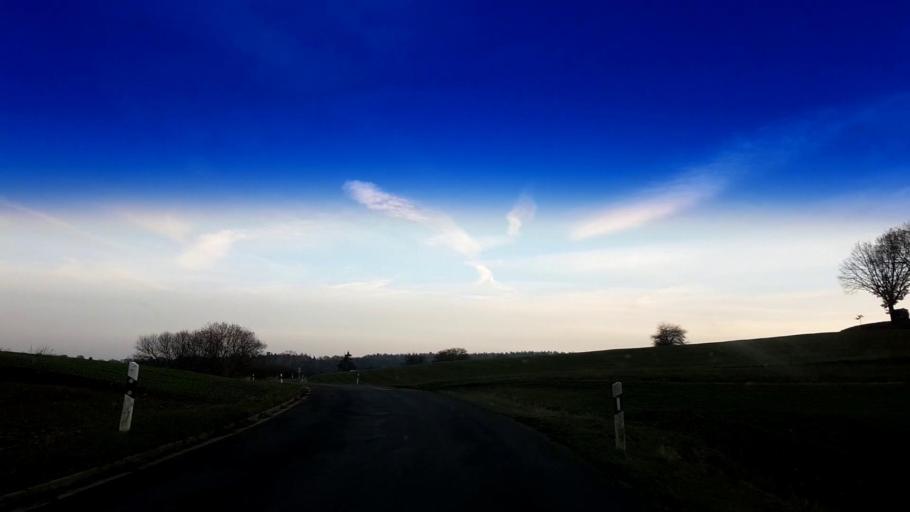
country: DE
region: Bavaria
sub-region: Upper Franconia
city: Stegaurach
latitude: 49.8626
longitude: 10.8207
